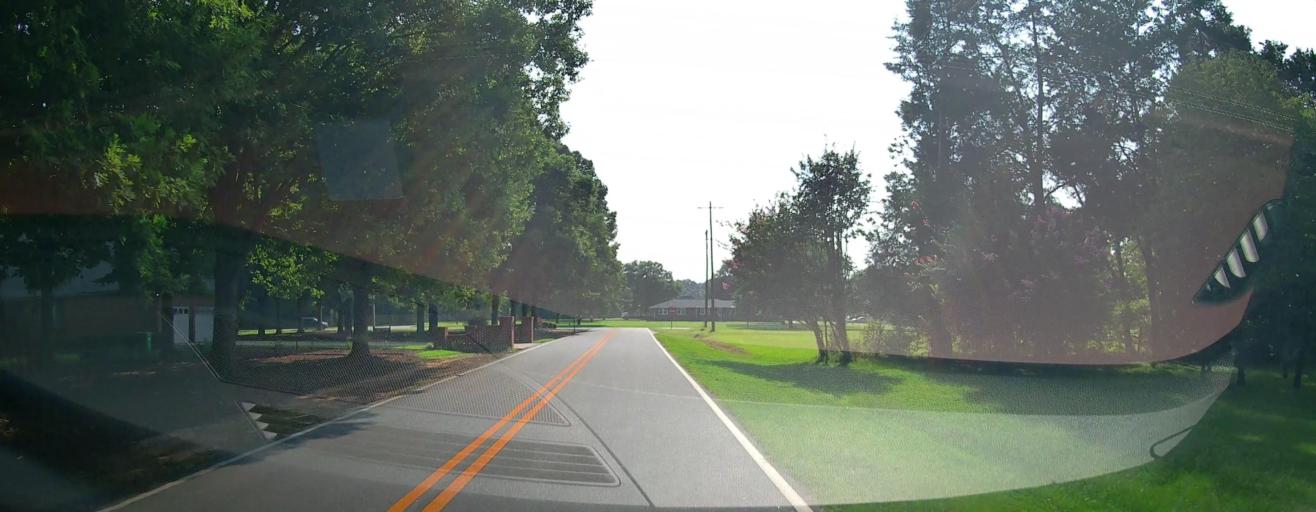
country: US
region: Georgia
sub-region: Houston County
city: Centerville
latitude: 32.6527
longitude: -83.6949
